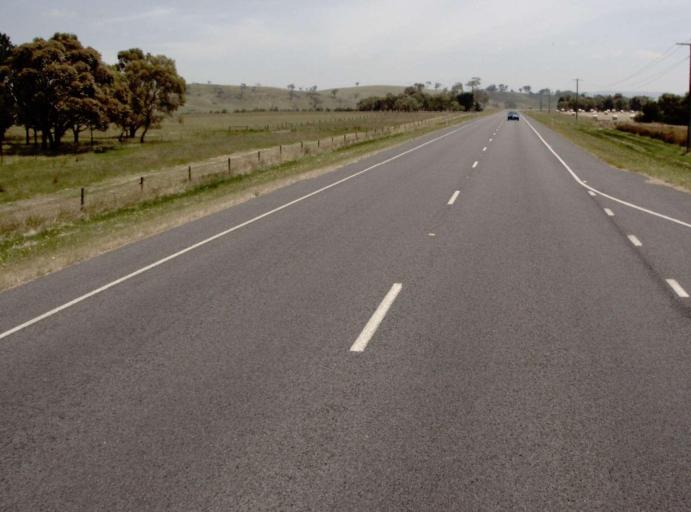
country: AU
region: Victoria
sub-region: Latrobe
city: Traralgon
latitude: -38.2380
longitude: 146.5431
